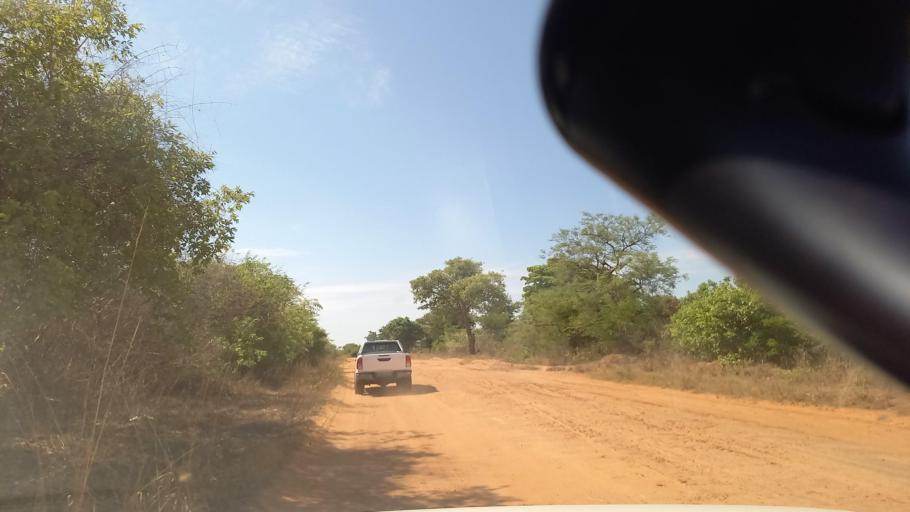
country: ZM
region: Southern
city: Mazabuka
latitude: -16.0366
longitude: 27.6177
